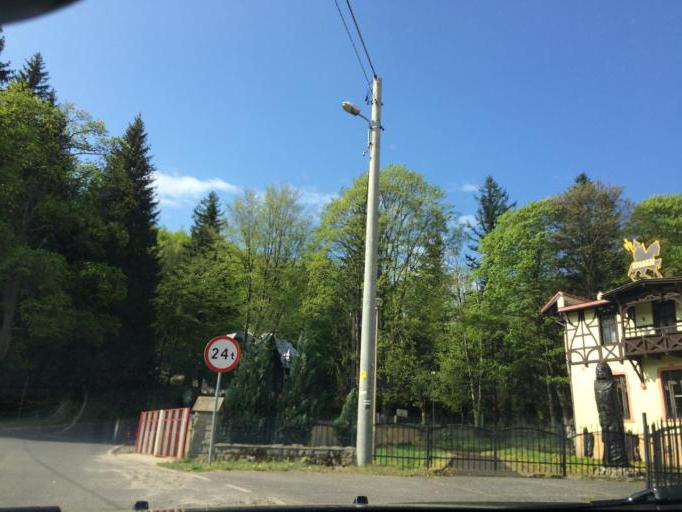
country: PL
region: Lower Silesian Voivodeship
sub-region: Powiat klodzki
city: Jugow
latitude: 50.6687
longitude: 16.5378
